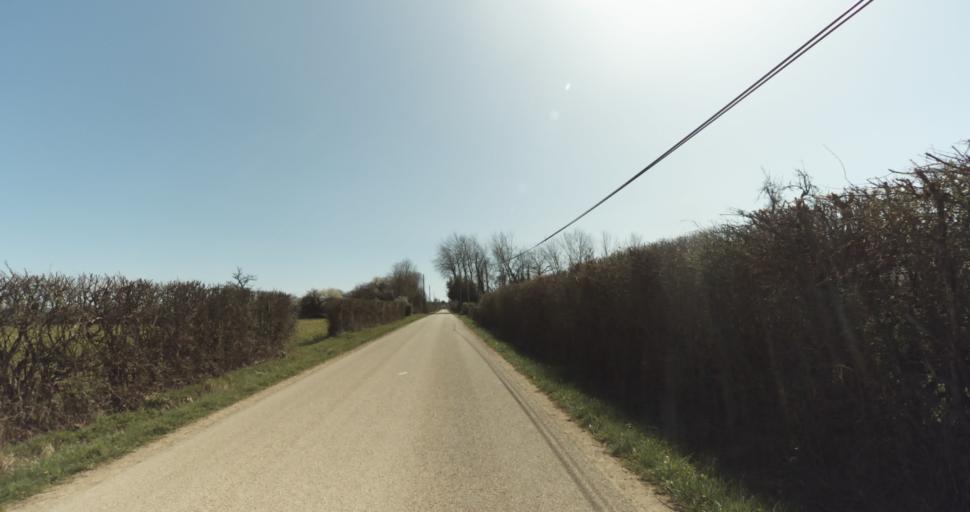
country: FR
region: Lower Normandy
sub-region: Departement du Calvados
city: Saint-Pierre-sur-Dives
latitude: 48.9802
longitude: -0.0103
